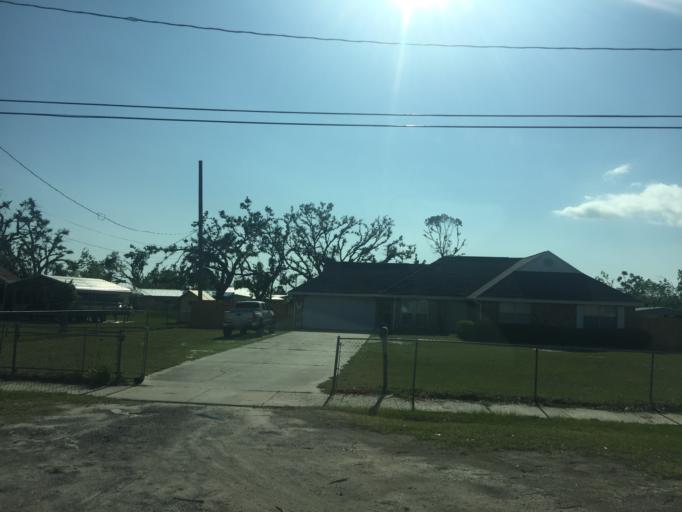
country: US
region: Florida
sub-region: Bay County
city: Springfield
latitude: 30.1583
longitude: -85.6165
